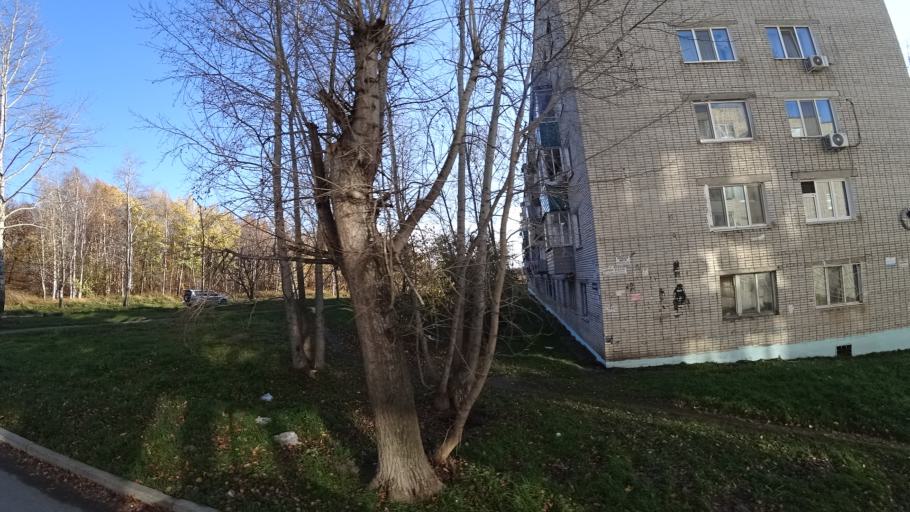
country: RU
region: Khabarovsk Krai
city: Amursk
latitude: 50.2302
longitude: 136.9117
